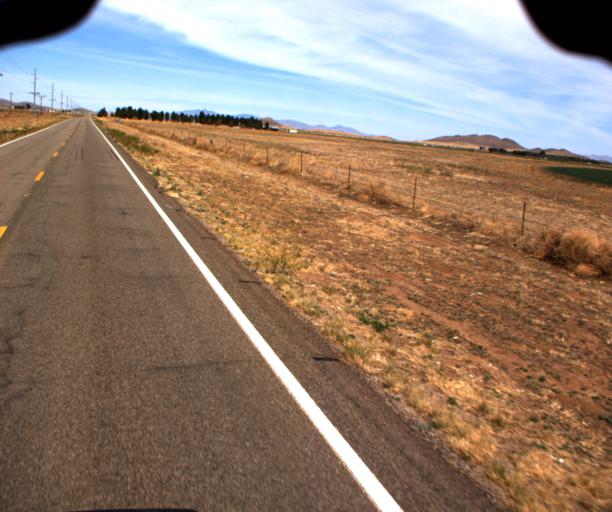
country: US
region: Arizona
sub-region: Cochise County
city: Tombstone
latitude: 31.8231
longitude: -109.6951
